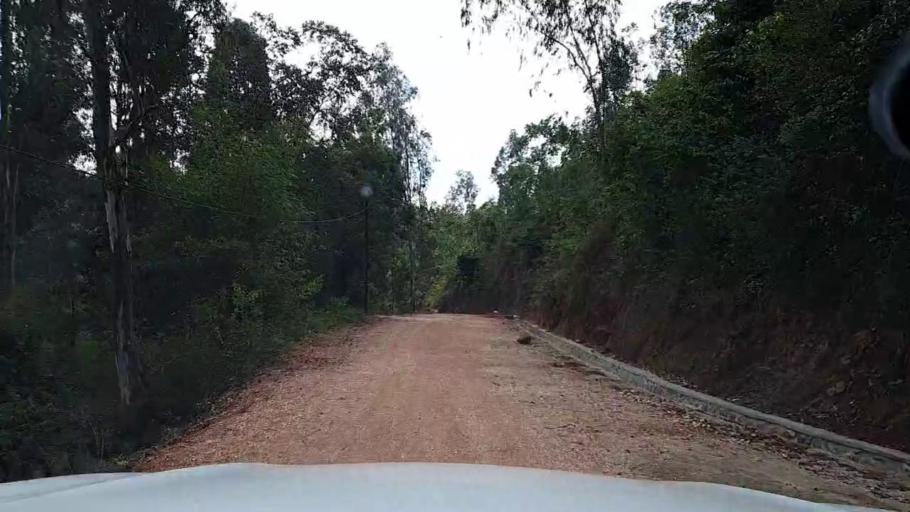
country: BI
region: Ngozi
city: Ngozi
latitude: -2.8114
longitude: 29.7305
